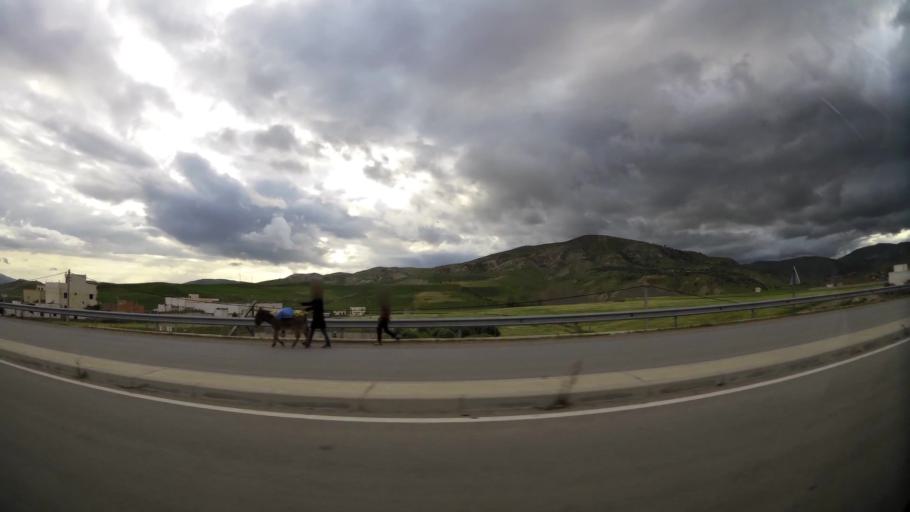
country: MA
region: Taza-Al Hoceima-Taounate
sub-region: Taza
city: Taza
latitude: 34.2646
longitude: -3.9578
